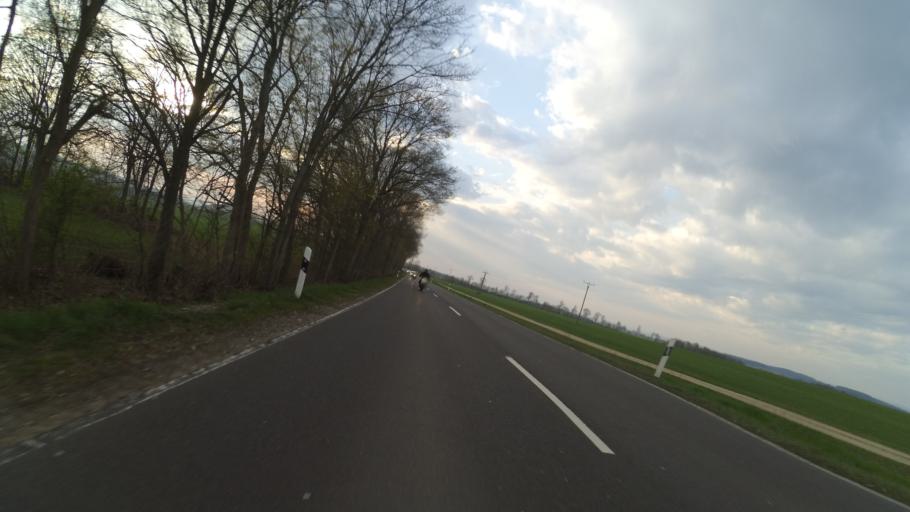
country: DE
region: Rheinland-Pfalz
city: Longkamp
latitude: 49.8816
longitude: 7.0995
